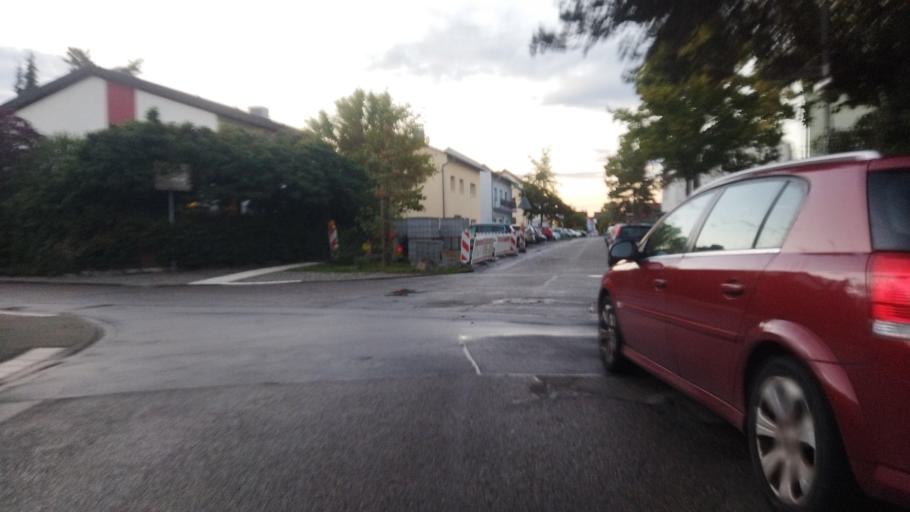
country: DE
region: Hesse
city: Lorsch
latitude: 49.6458
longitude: 8.5717
